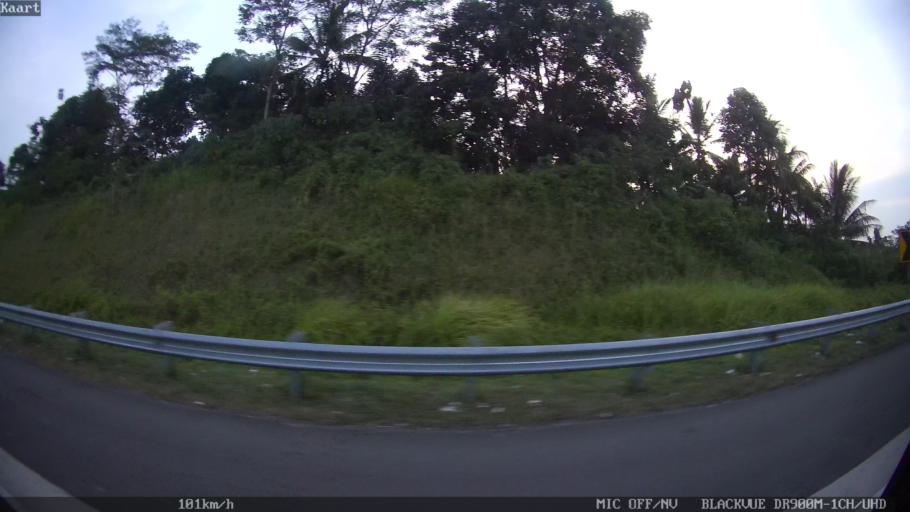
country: ID
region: Lampung
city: Penengahan
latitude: -5.7735
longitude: 105.7173
